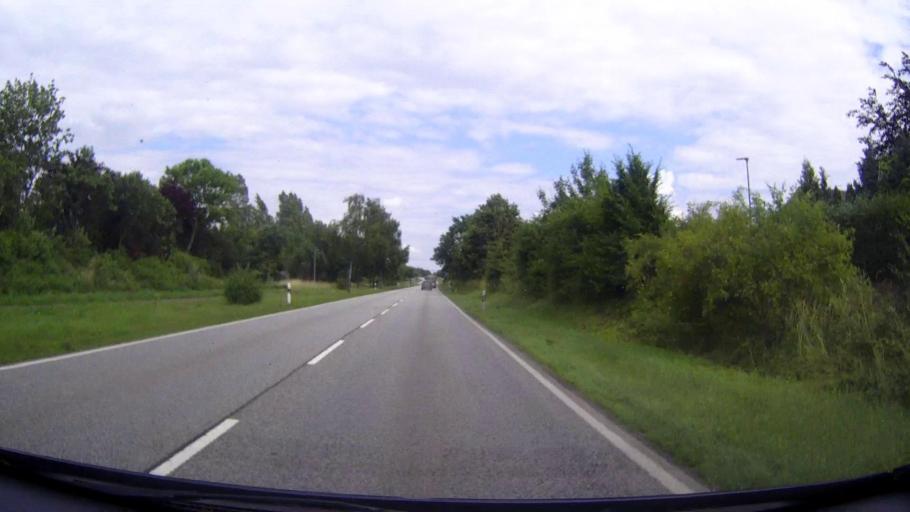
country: DE
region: Schleswig-Holstein
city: Wasbek
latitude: 54.0703
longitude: 9.9120
